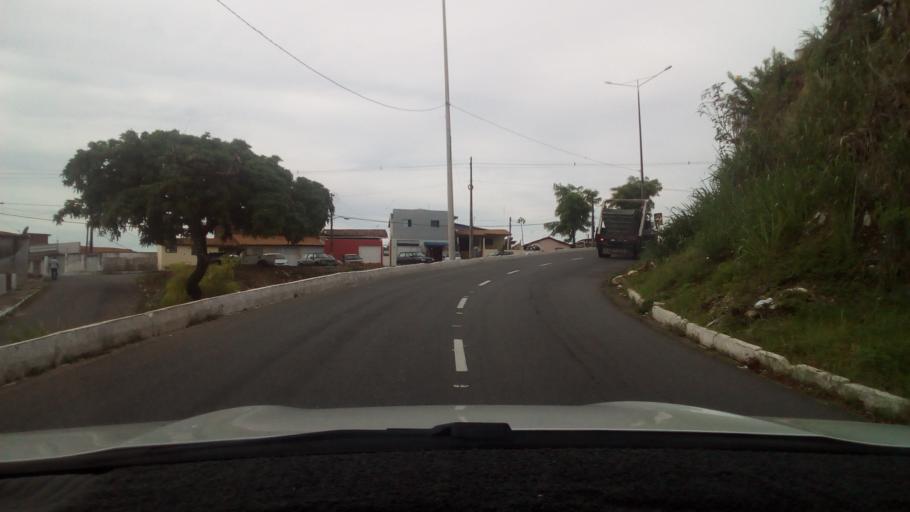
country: BR
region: Paraiba
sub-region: Joao Pessoa
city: Joao Pessoa
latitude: -7.1109
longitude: -34.8823
